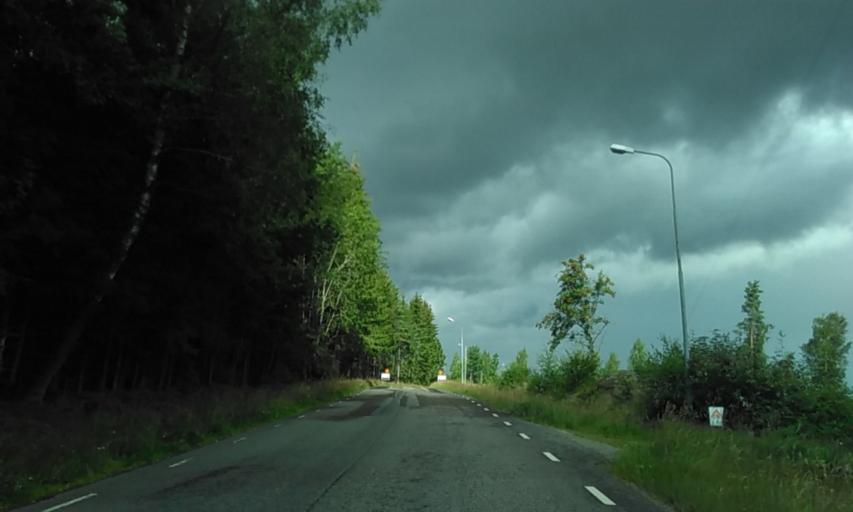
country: SE
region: Vaestra Goetaland
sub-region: Vargarda Kommun
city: Jonstorp
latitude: 58.0053
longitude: 12.7154
